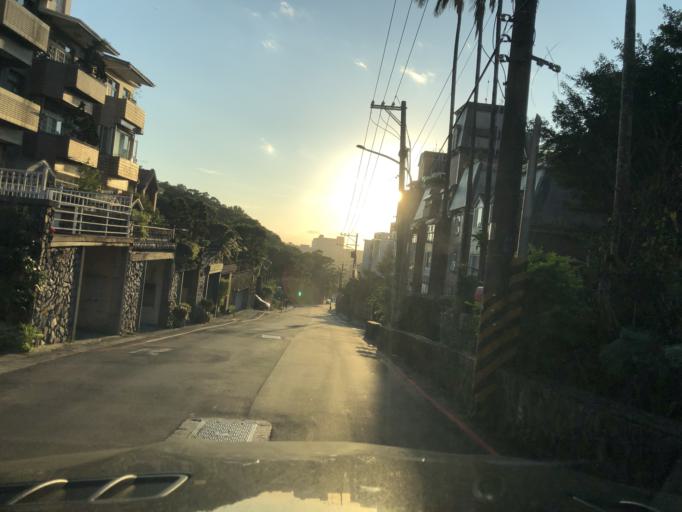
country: TW
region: Taipei
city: Taipei
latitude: 25.1398
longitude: 121.5510
